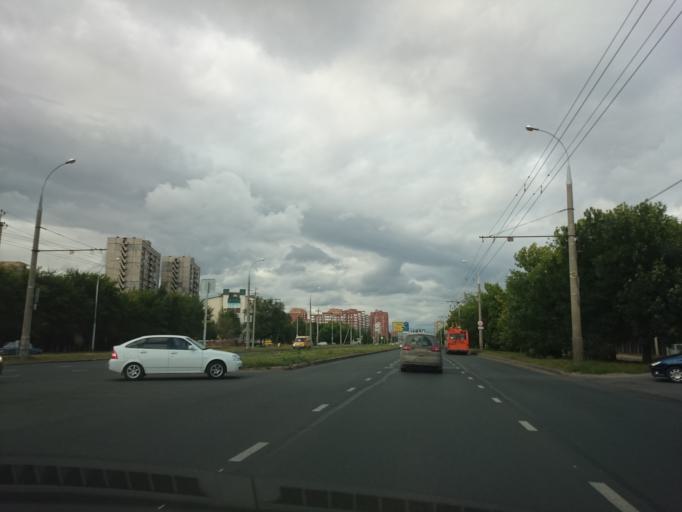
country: RU
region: Samara
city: Tol'yatti
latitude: 53.5091
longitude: 49.3034
